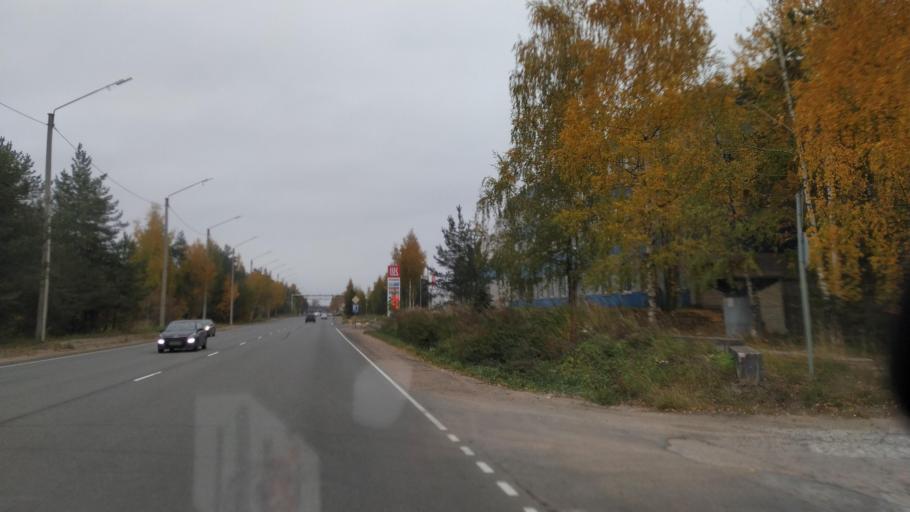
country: RU
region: Leningrad
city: Sosnovyy Bor
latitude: 59.8729
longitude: 29.0854
